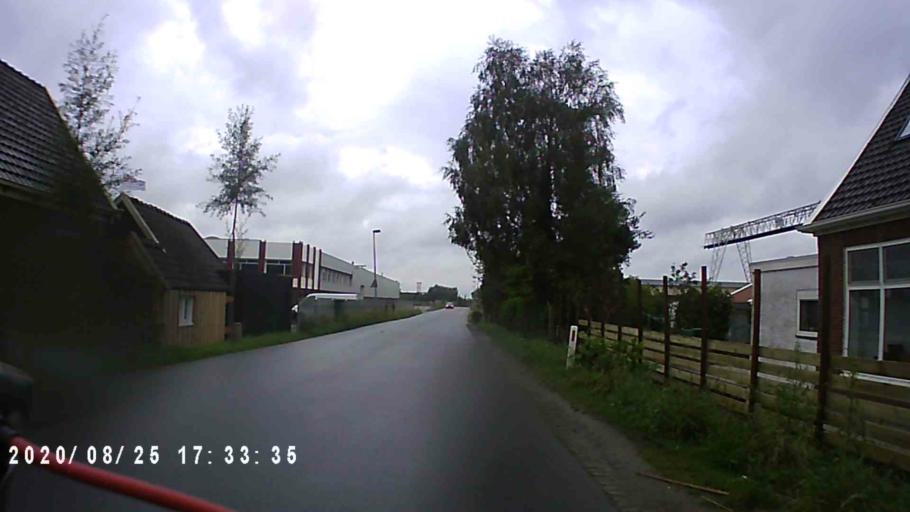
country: NL
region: Groningen
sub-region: Gemeente Zuidhorn
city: Aduard
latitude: 53.2143
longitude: 6.4883
